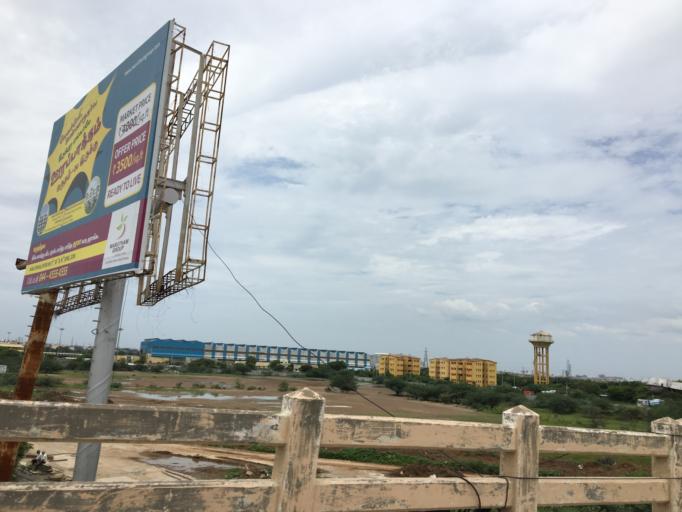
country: IN
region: Tamil Nadu
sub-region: Kancheepuram
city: Madipakkam
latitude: 12.9669
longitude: 80.2175
